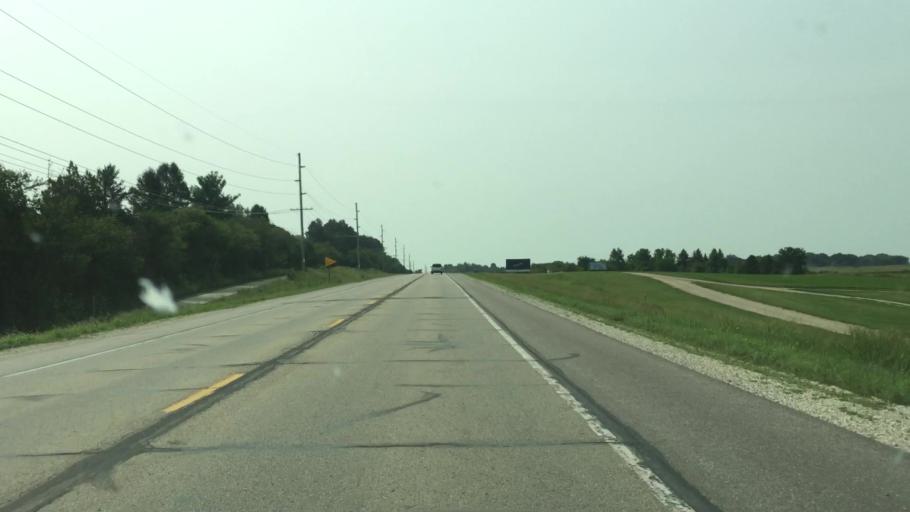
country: US
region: Iowa
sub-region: Dickinson County
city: Milford
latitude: 43.3531
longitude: -95.1799
